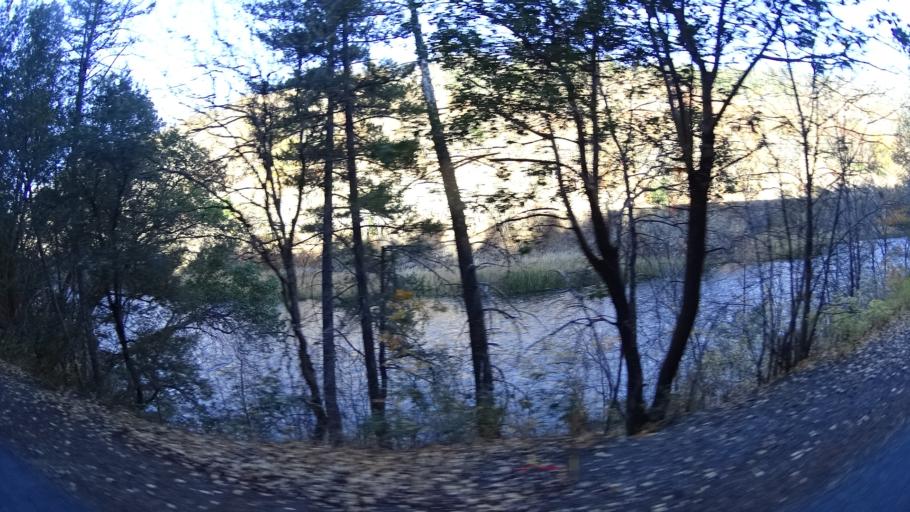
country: US
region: California
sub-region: Siskiyou County
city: Yreka
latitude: 41.8428
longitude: -122.9103
